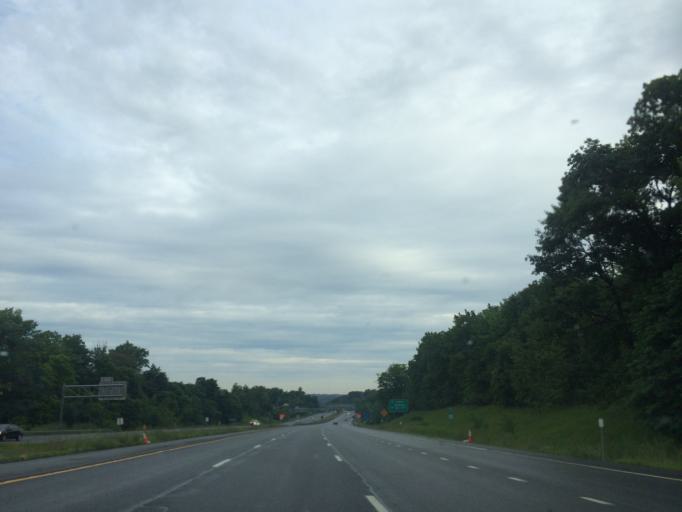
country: US
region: New York
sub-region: Rensselaer County
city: Rensselaer
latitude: 42.6546
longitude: -73.7175
